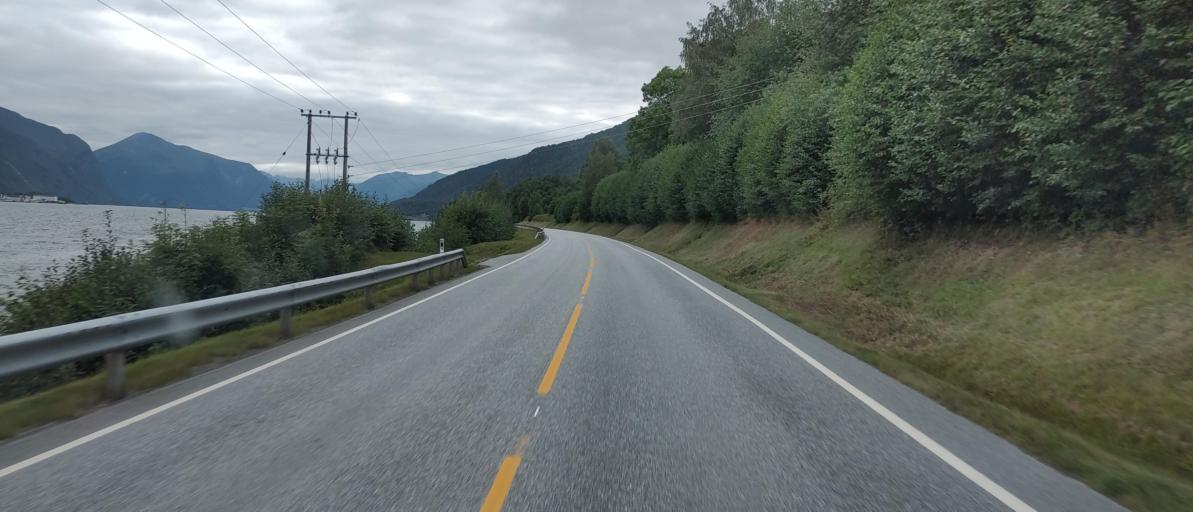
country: NO
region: More og Romsdal
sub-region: Rauma
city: Andalsnes
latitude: 62.5847
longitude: 7.7282
